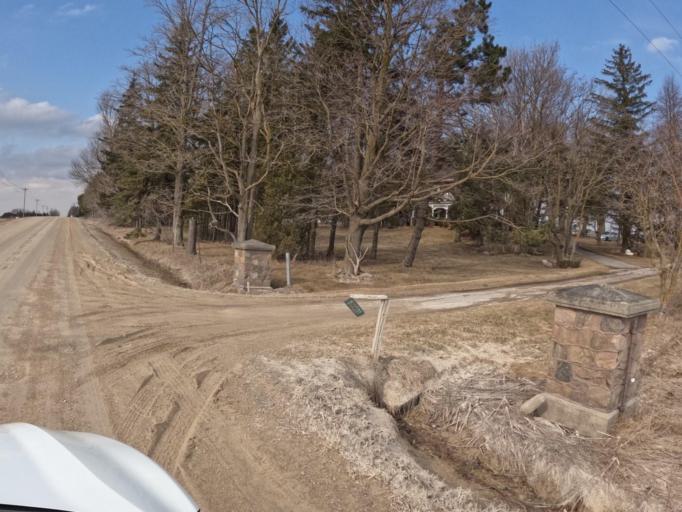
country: CA
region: Ontario
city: Orangeville
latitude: 43.8802
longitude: -80.2967
